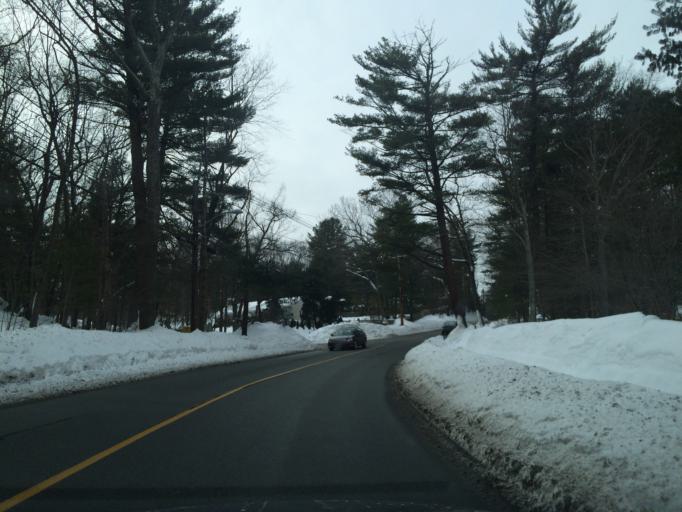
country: US
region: Massachusetts
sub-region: Norfolk County
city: Wellesley
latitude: 42.3260
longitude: -71.3101
